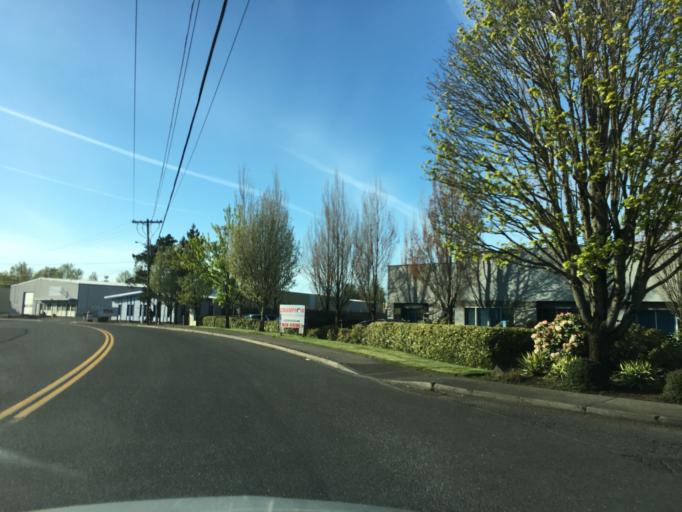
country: US
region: Oregon
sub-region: Multnomah County
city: Lents
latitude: 45.5598
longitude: -122.5291
